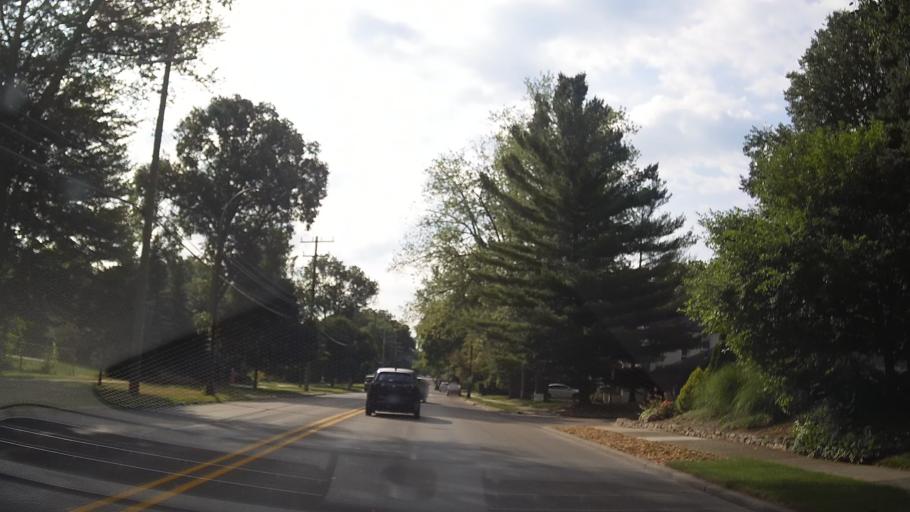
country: US
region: Michigan
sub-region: Wayne County
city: Grosse Pointe Farms
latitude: 42.4140
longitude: -82.9032
